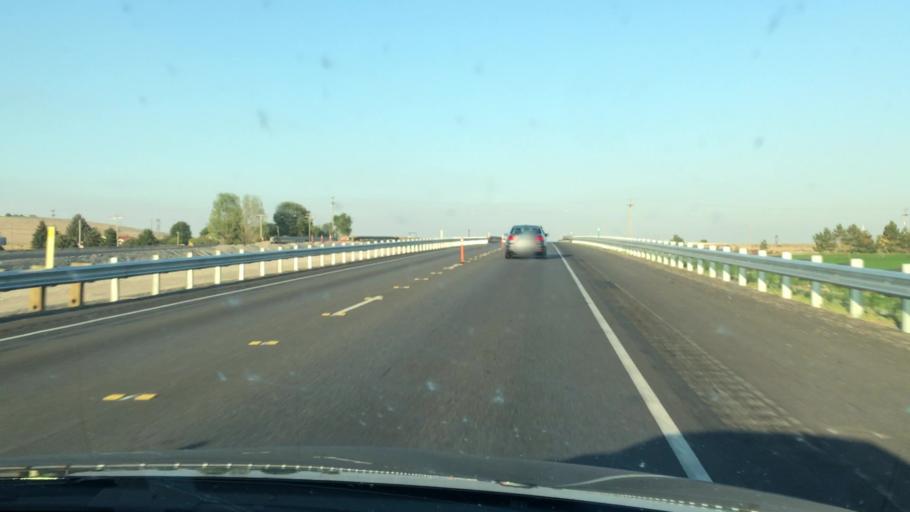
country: US
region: Idaho
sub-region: Twin Falls County
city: Hansen
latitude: 42.5761
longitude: -114.2533
